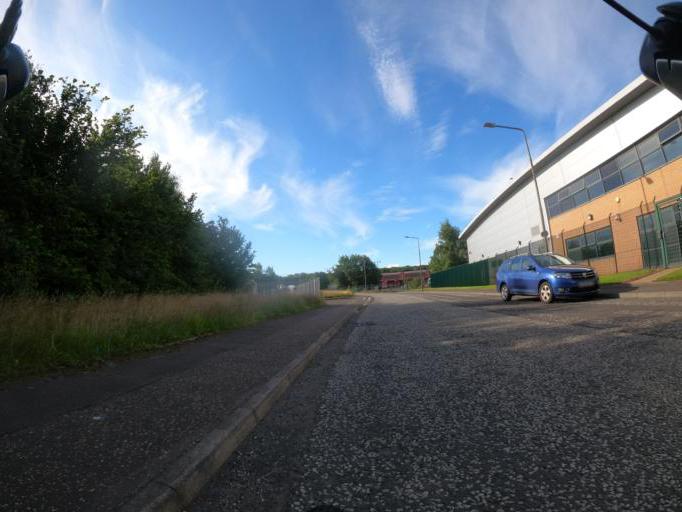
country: GB
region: Scotland
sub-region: Edinburgh
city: Newbridge
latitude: 55.9367
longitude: -3.4070
